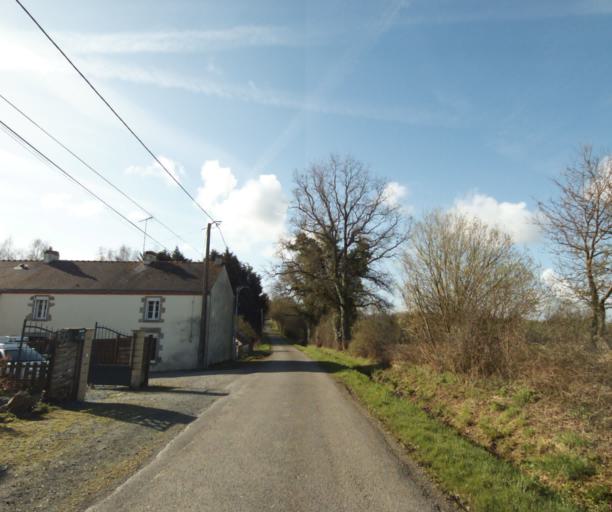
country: FR
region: Pays de la Loire
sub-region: Departement de la Loire-Atlantique
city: Bouvron
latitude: 47.4032
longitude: -1.8488
